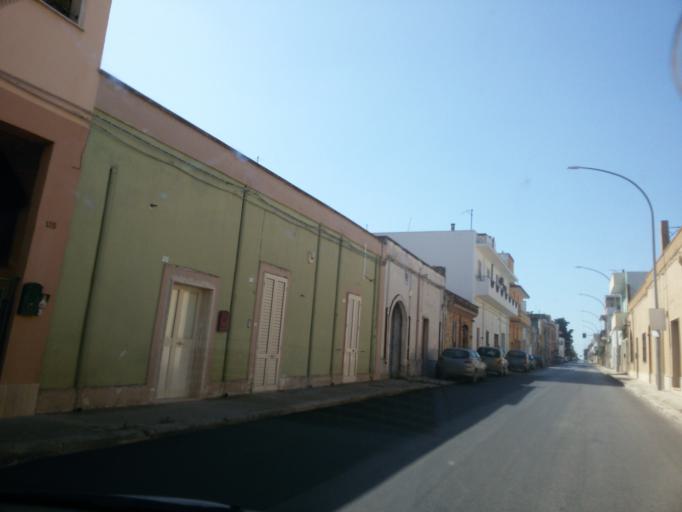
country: IT
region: Apulia
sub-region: Provincia di Brindisi
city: San Donaci
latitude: 40.4496
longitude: 17.9210
